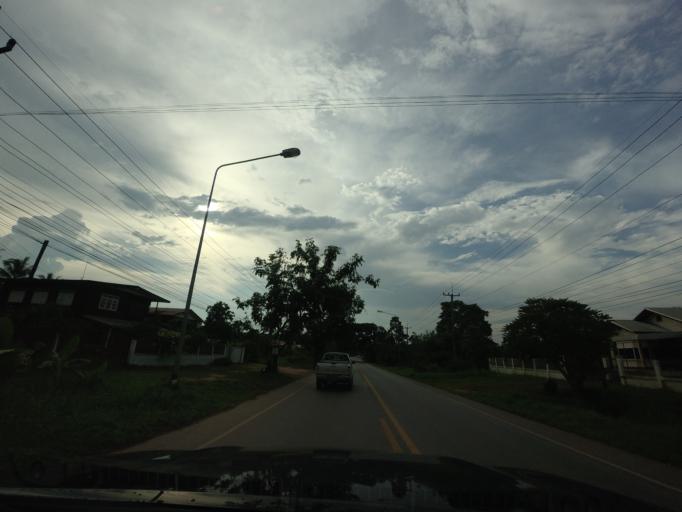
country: TH
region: Changwat Udon Thani
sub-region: Amphoe Ban Phue
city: Ban Phue
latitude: 17.7041
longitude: 102.4325
